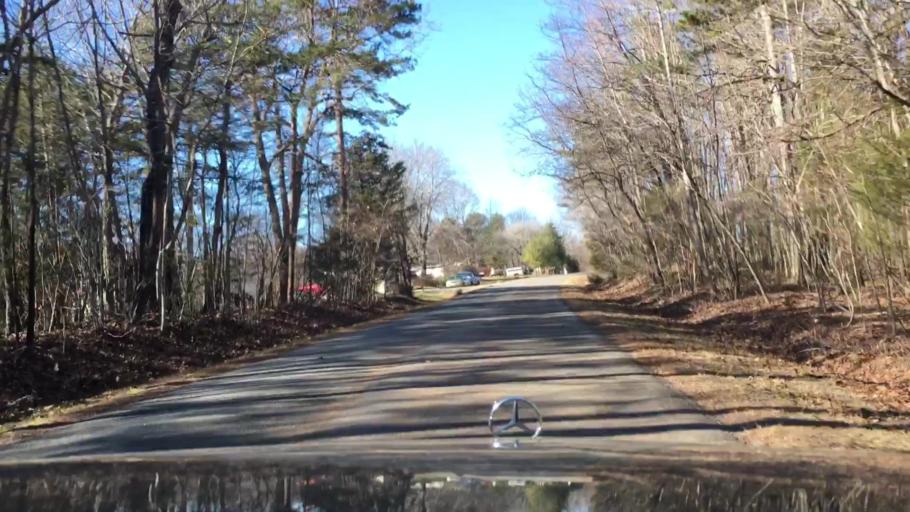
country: US
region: Virginia
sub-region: Campbell County
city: Altavista
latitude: 37.1784
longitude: -79.3128
